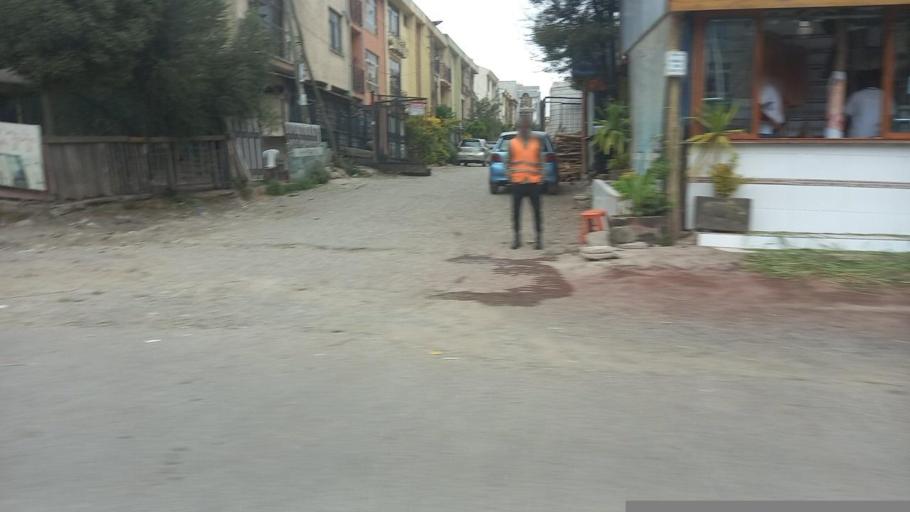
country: ET
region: Adis Abeba
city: Addis Ababa
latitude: 9.0099
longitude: 38.8551
